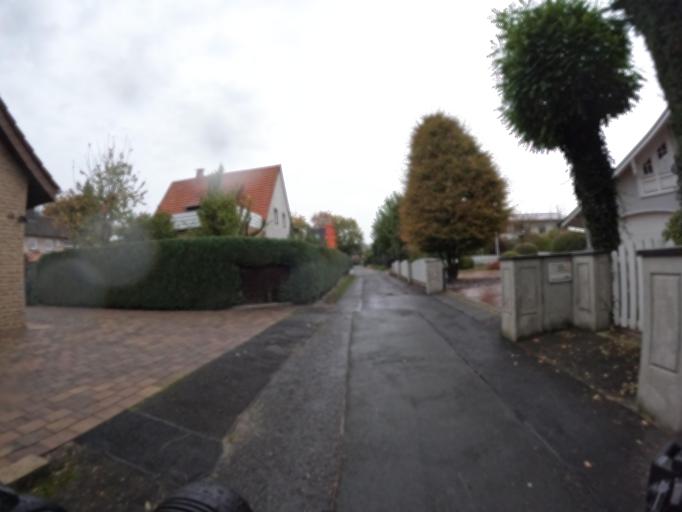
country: DE
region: North Rhine-Westphalia
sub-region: Regierungsbezirk Detmold
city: Hovelhof
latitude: 51.8178
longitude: 8.6644
